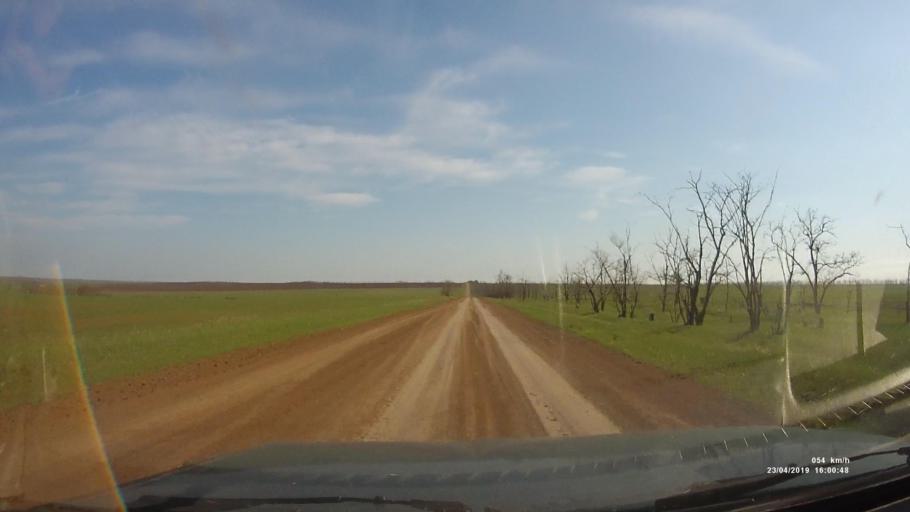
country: RU
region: Rostov
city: Remontnoye
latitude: 46.5064
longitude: 43.1070
